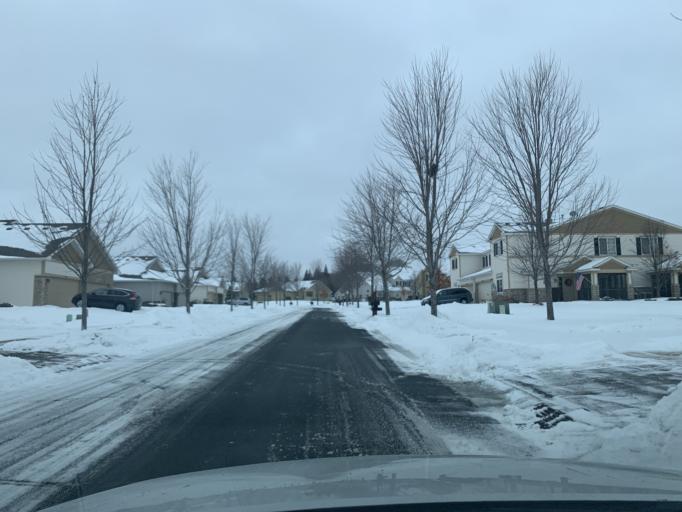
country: US
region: Minnesota
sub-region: Carver County
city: Victoria
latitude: 44.8397
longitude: -93.6546
